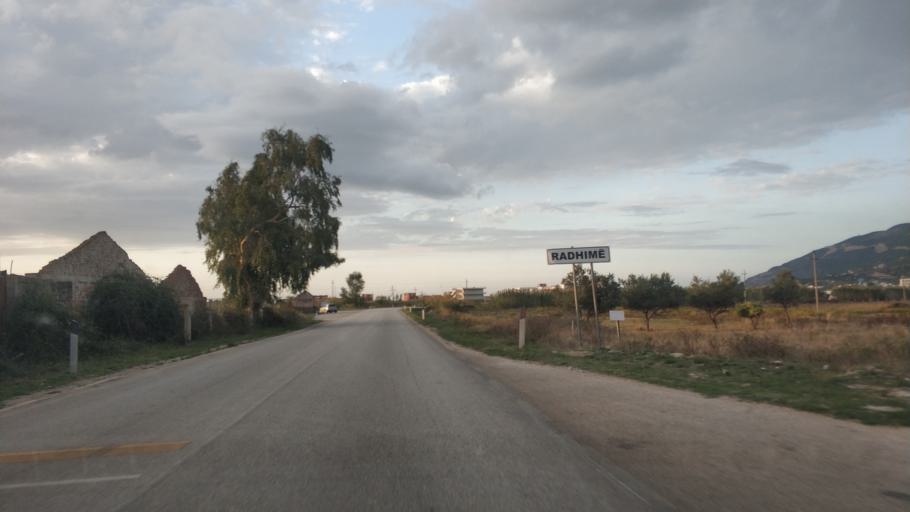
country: AL
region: Vlore
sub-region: Rrethi i Vlores
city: Orikum
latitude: 40.3334
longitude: 19.4777
